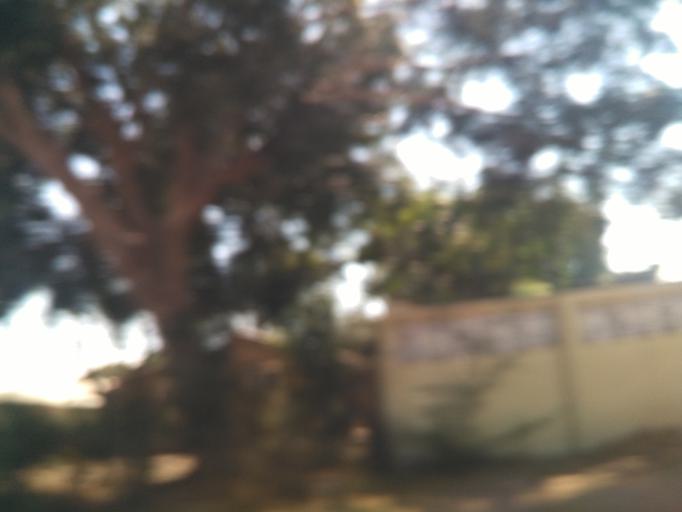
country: TZ
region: Dodoma
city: Dodoma
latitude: -6.1676
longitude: 35.7508
